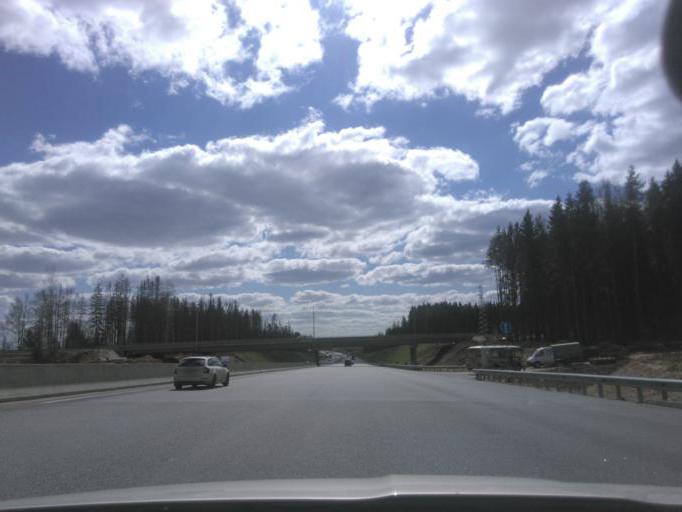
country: RU
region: Moskovskaya
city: Skhodnya
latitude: 55.9826
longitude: 37.3114
